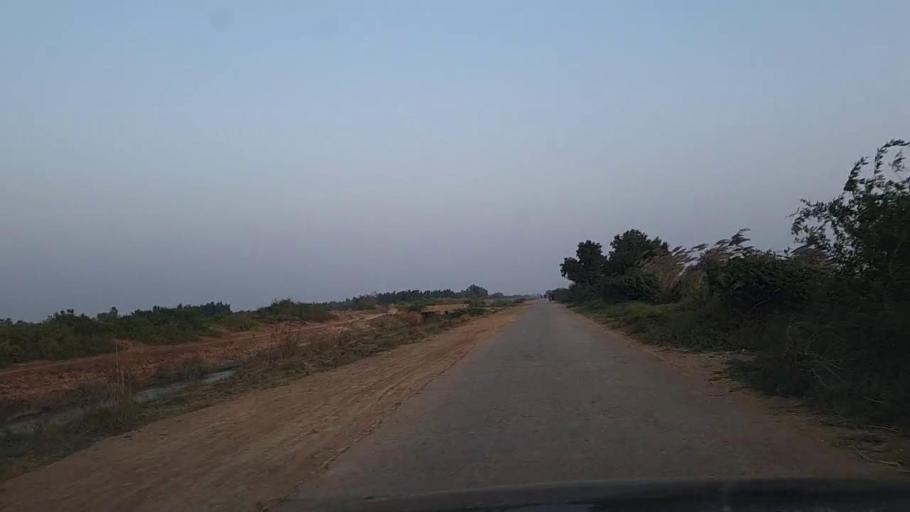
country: PK
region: Sindh
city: Mirpur Sakro
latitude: 24.6336
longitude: 67.6176
